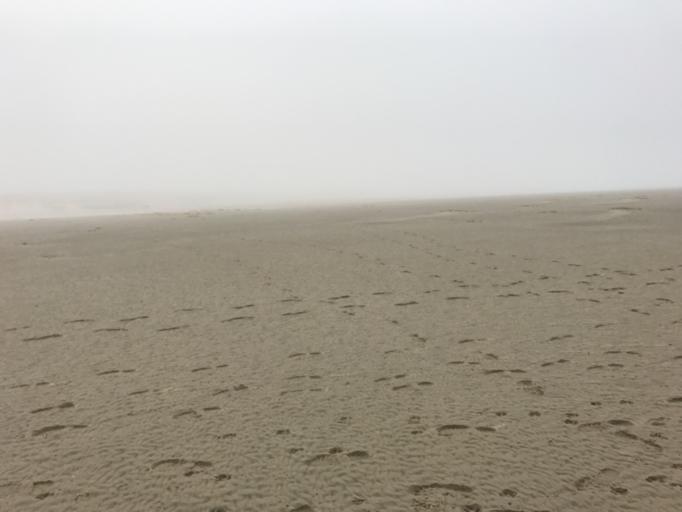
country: DE
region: Lower Saxony
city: Borkum
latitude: 53.6090
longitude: 6.7047
